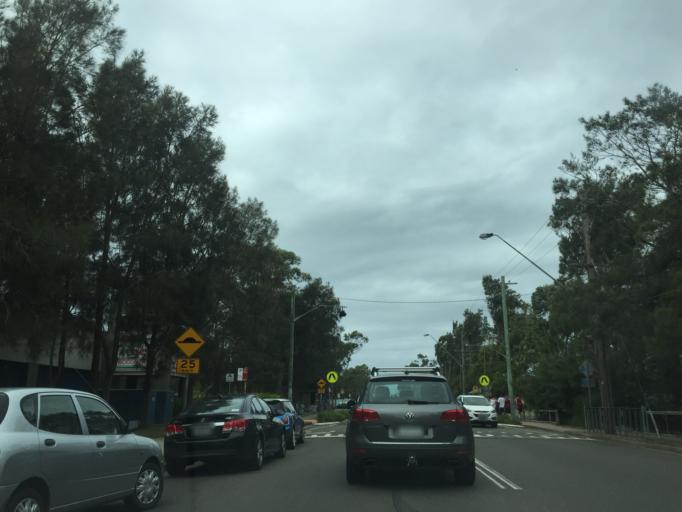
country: AU
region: New South Wales
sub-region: Pittwater
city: Warriewood
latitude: -33.6969
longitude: 151.2950
